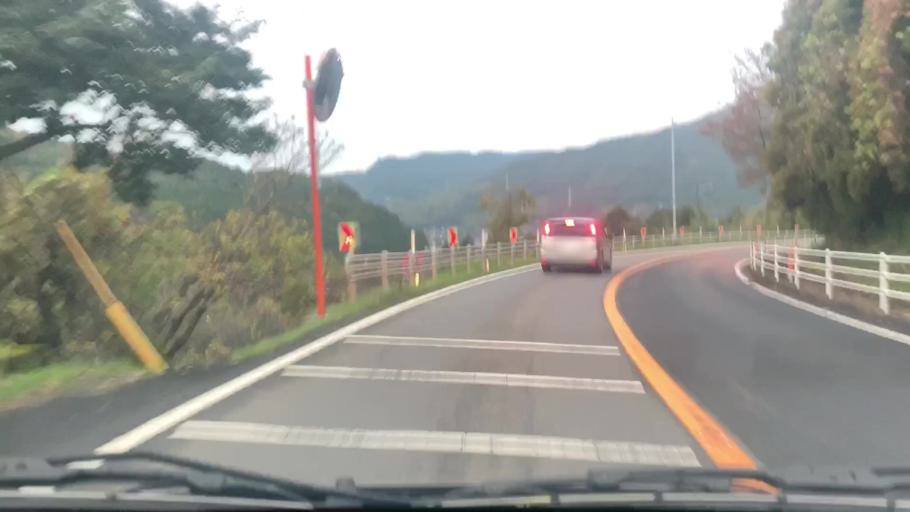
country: JP
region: Saga Prefecture
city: Ureshinomachi-shimojuku
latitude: 33.0523
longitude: 129.9384
